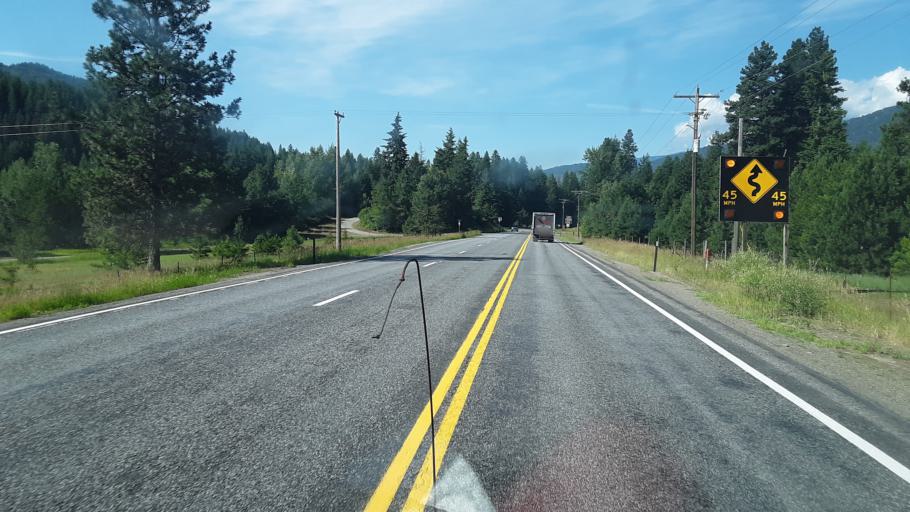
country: US
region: Idaho
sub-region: Boundary County
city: Bonners Ferry
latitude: 48.5234
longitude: -116.4377
